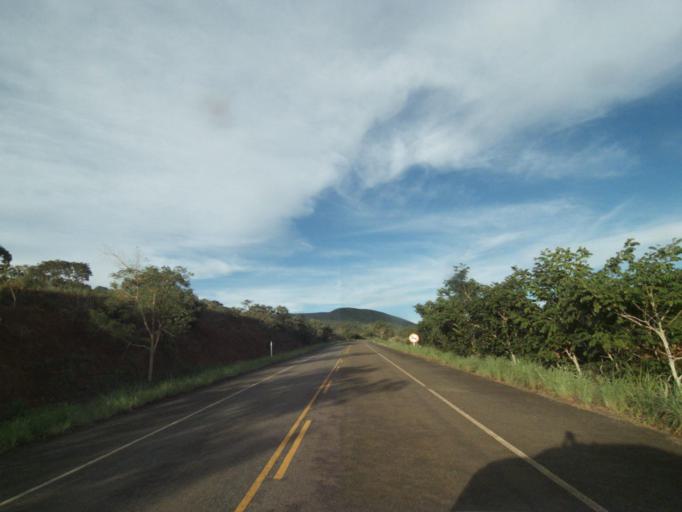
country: BR
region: Goias
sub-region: Jaragua
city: Jaragua
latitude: -15.8414
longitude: -49.3264
